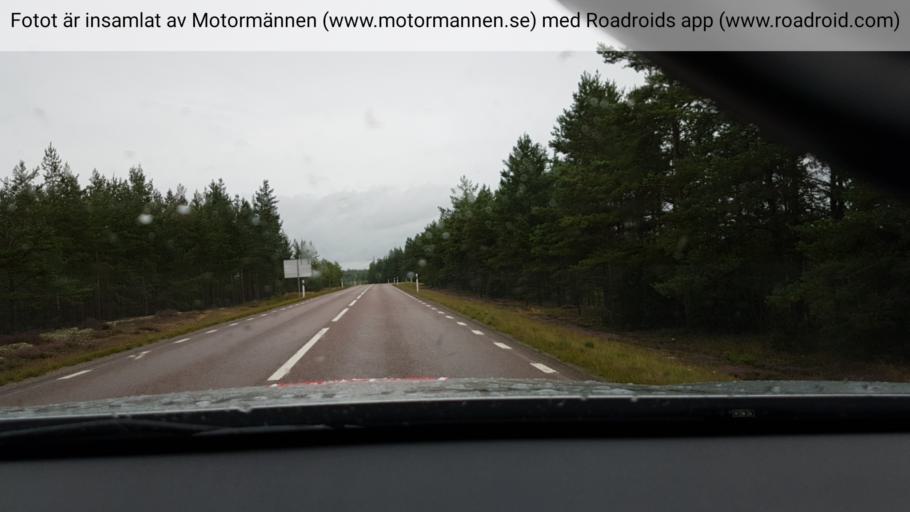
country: SE
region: Gaevleborg
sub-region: Gavle Kommun
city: Valbo
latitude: 60.5994
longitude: 16.9752
